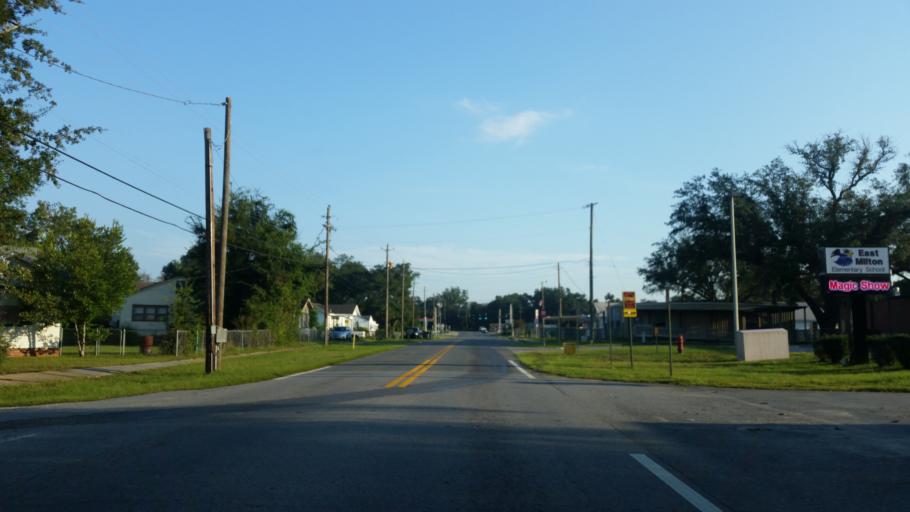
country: US
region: Florida
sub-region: Santa Rosa County
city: East Milton
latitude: 30.6218
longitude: -87.0213
